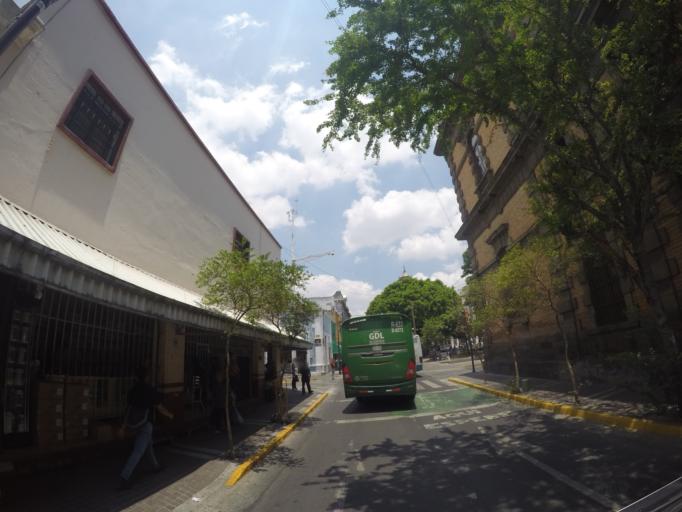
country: MX
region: Jalisco
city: Guadalajara
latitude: 20.6795
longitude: -103.3496
